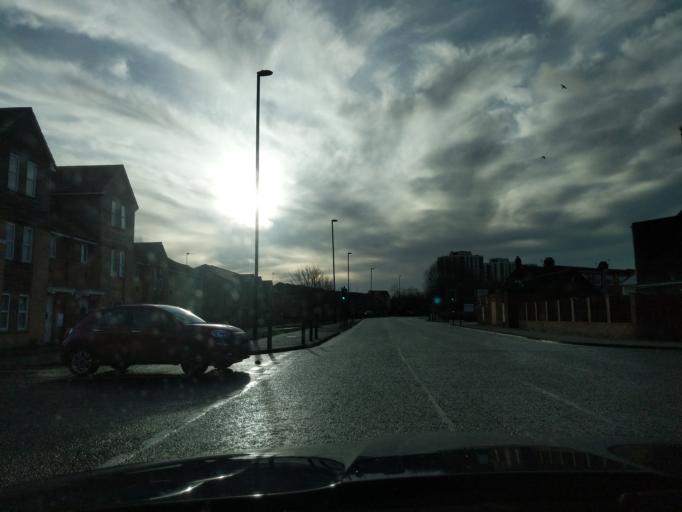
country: GB
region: England
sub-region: Borough of North Tyneside
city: Wallsend
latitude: 54.9702
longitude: -1.5417
